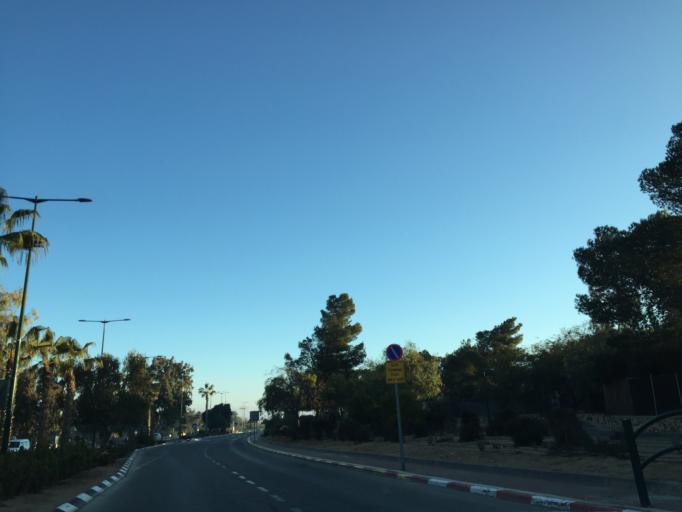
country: IL
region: Southern District
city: Mitzpe Ramon
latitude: 30.6113
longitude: 34.8025
